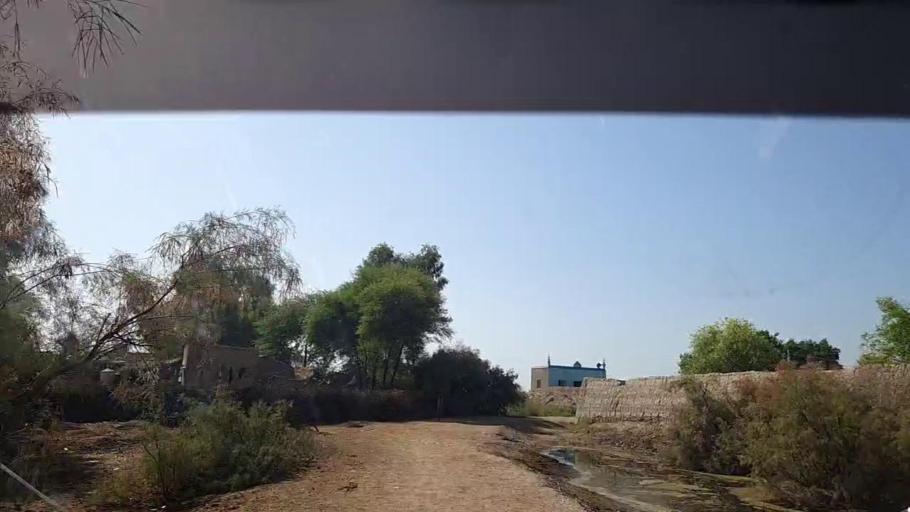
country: PK
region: Sindh
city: Ghauspur
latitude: 28.1802
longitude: 69.0272
